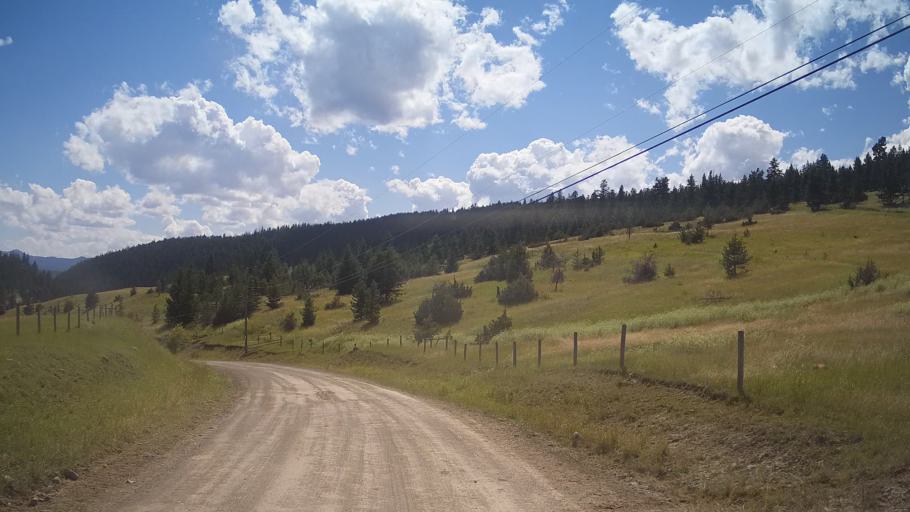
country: CA
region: British Columbia
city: Lillooet
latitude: 51.3075
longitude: -121.9871
